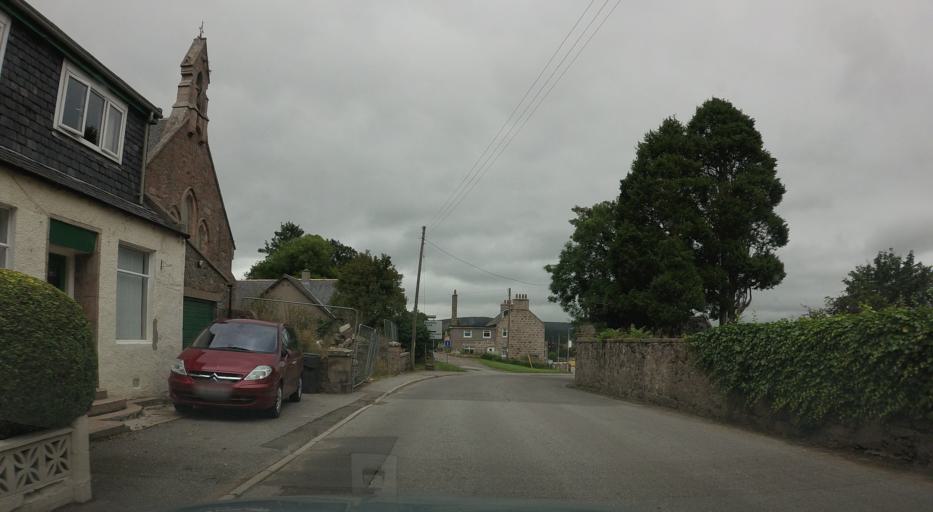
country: GB
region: Scotland
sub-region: Aberdeenshire
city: Banchory
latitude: 57.0205
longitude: -2.5384
